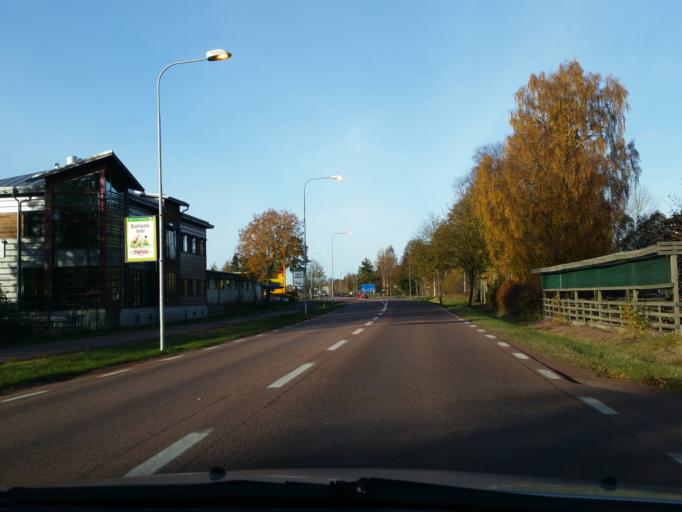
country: AX
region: Mariehamns stad
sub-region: Mariehamn
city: Mariehamn
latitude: 60.1100
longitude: 19.9304
